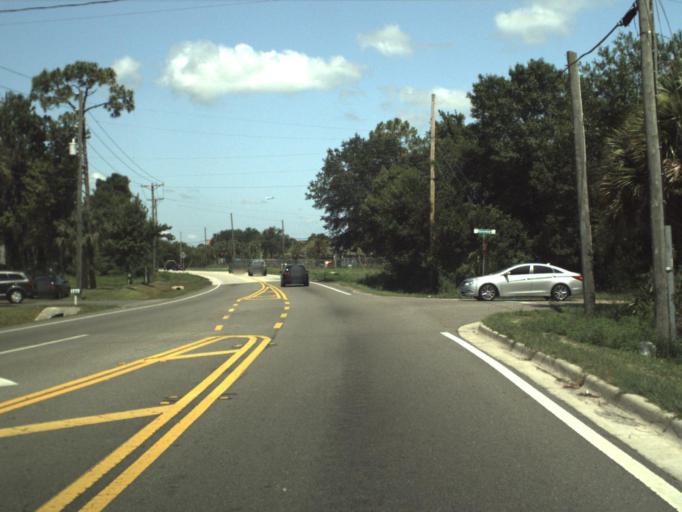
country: US
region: Florida
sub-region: Orange County
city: Conway
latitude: 28.4805
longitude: -81.2898
